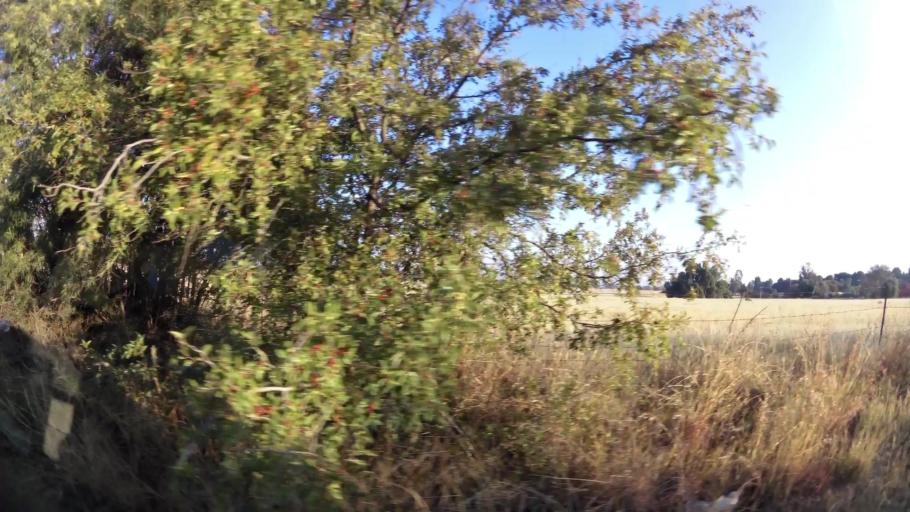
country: ZA
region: Orange Free State
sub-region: Mangaung Metropolitan Municipality
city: Bloemfontein
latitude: -29.0789
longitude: 26.1496
